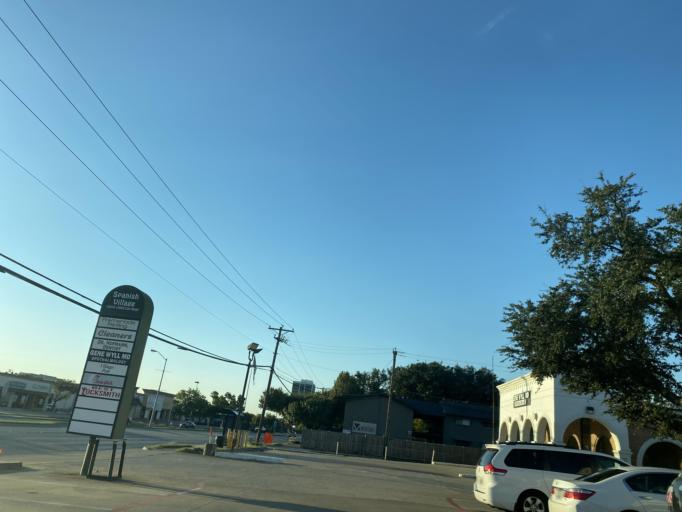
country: US
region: Texas
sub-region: Dallas County
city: Richardson
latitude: 32.9615
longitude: -96.7692
